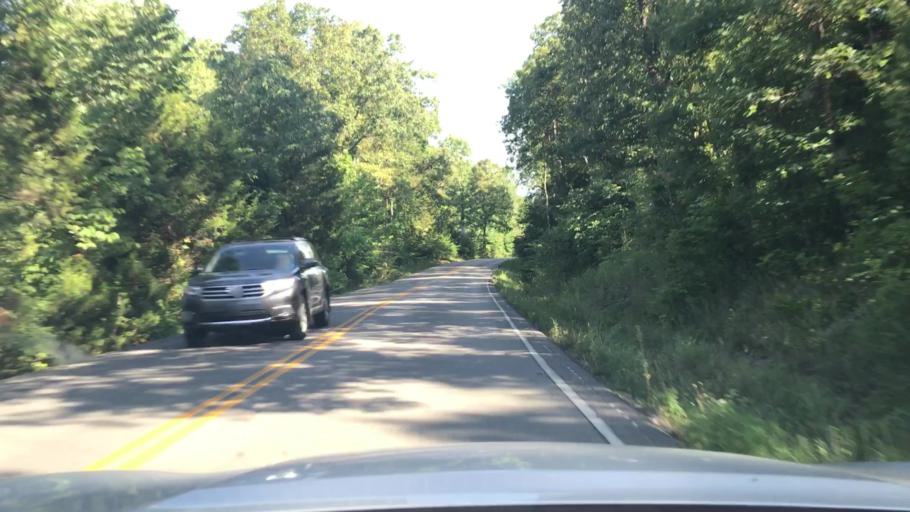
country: US
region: Kentucky
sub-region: Muhlenberg County
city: Greenville
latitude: 37.1347
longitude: -87.1431
